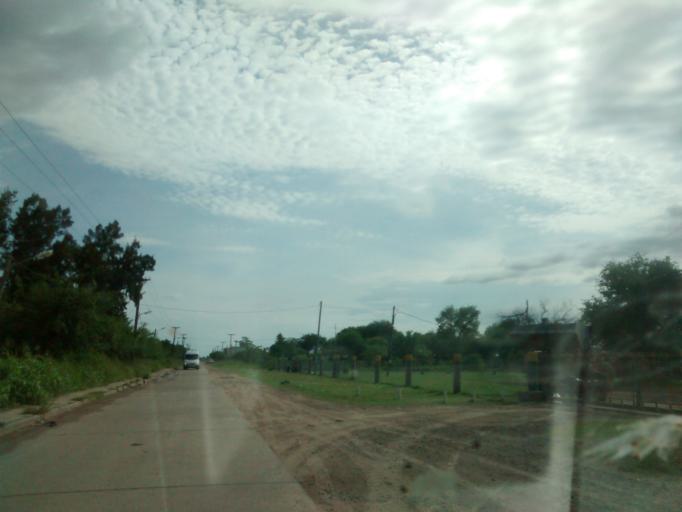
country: AR
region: Chaco
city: Resistencia
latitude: -27.4144
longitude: -58.9662
